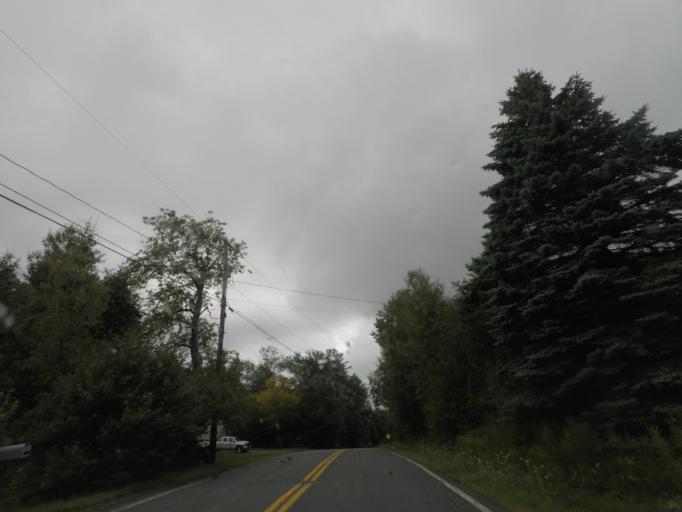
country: US
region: New York
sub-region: Rensselaer County
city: Poestenkill
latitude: 42.6880
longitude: -73.4396
